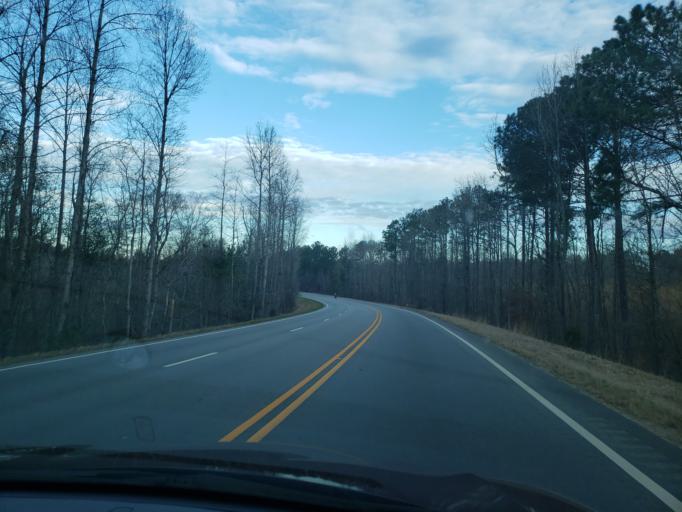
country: US
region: Alabama
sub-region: Randolph County
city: Roanoke
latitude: 33.2197
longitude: -85.4202
